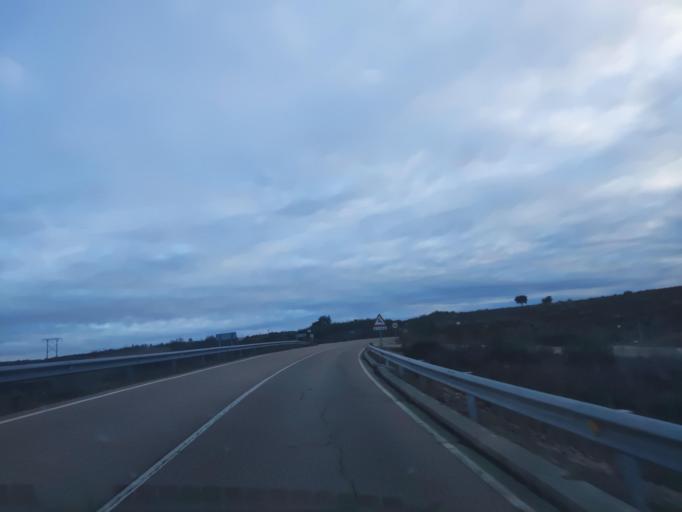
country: ES
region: Castille and Leon
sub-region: Provincia de Salamanca
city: Castillejo de Martin Viejo
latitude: 40.7038
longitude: -6.6482
